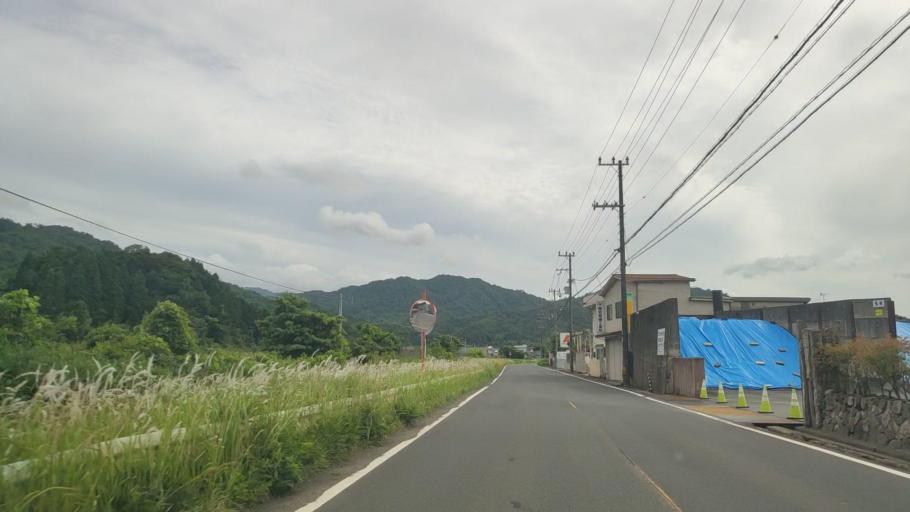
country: JP
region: Kyoto
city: Miyazu
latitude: 35.5572
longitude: 135.1645
